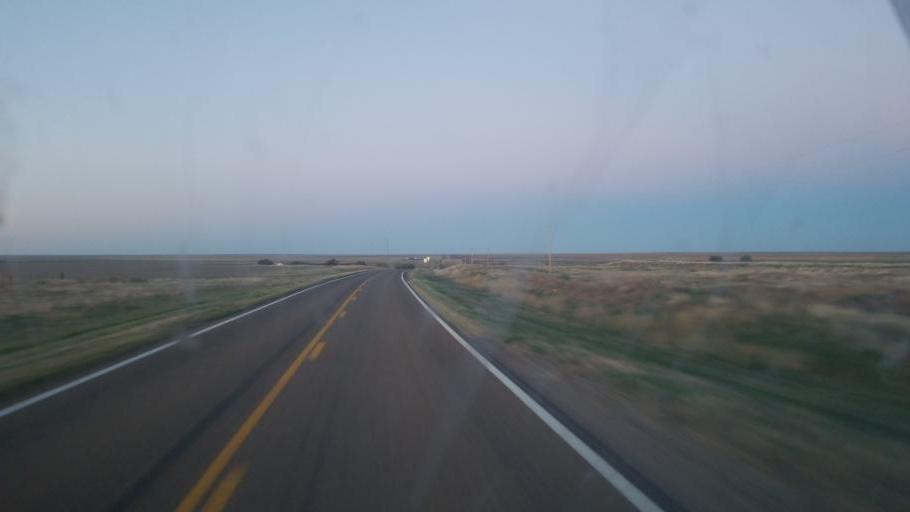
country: US
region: Kansas
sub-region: Wallace County
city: Sharon Springs
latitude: 38.9732
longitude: -101.4429
